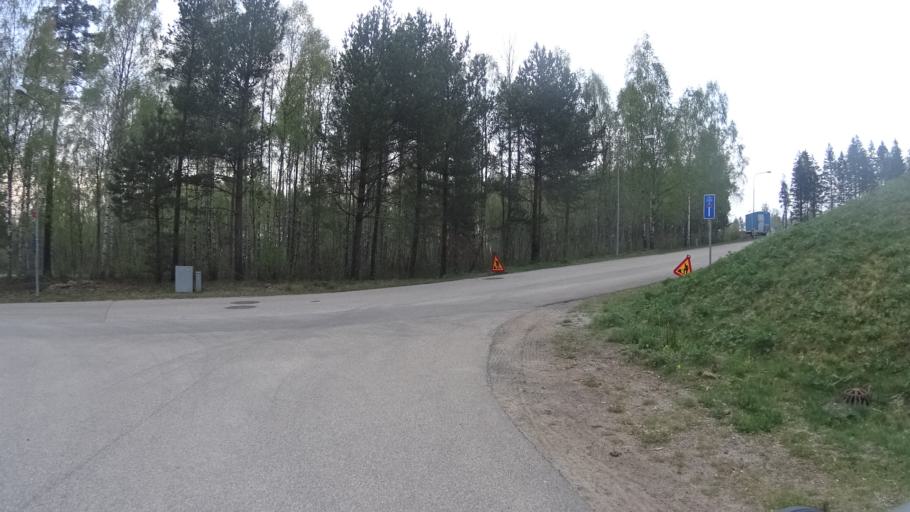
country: SE
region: Kronoberg
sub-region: Ljungby Kommun
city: Ljungby
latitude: 56.8368
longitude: 13.9729
